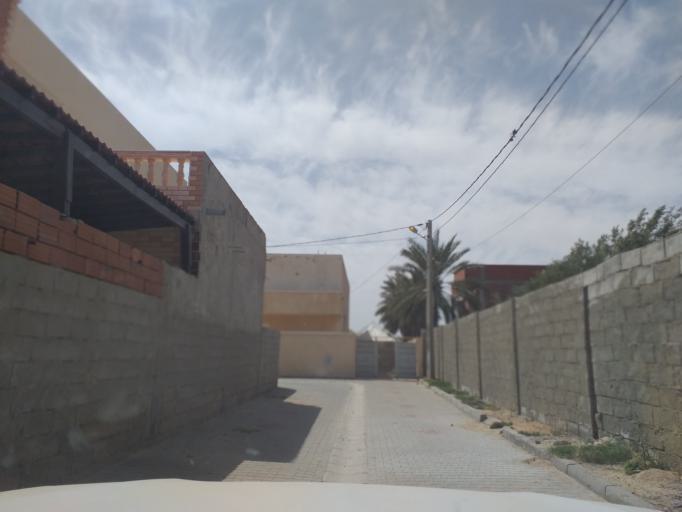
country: TN
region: Qabis
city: Gabes
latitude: 33.9498
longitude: 10.0665
